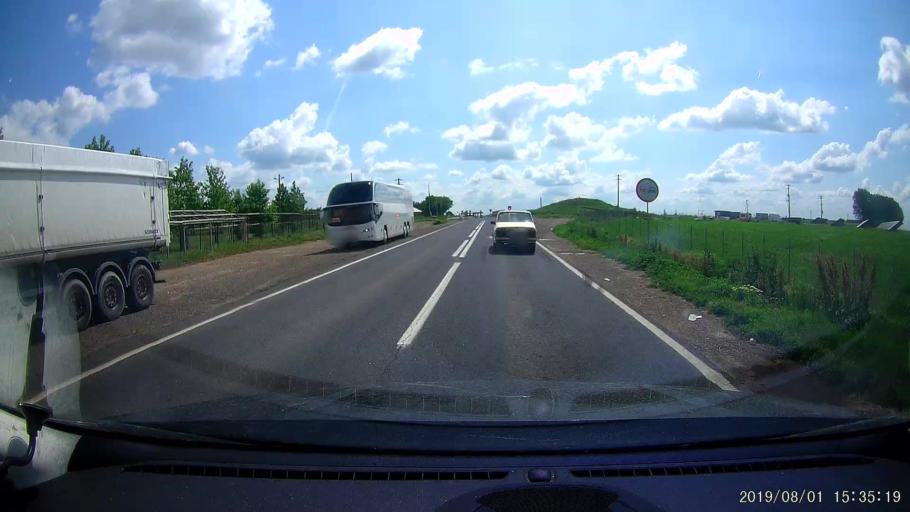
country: RO
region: Braila
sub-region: Comuna Insuratei
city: Insuratei
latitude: 44.9072
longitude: 27.5936
